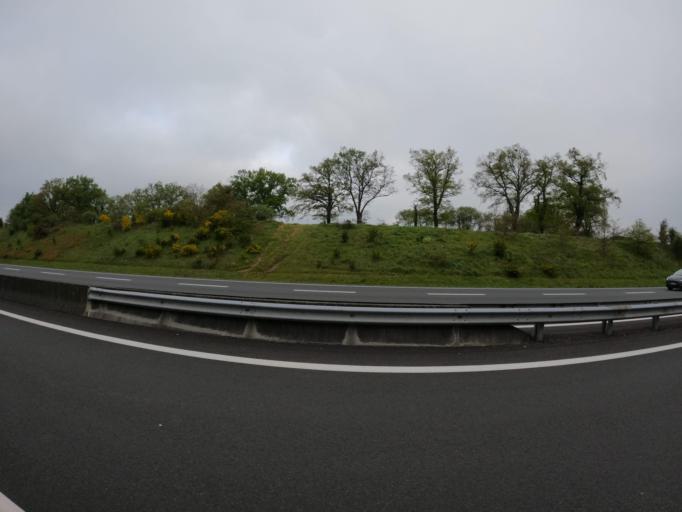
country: FR
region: Pays de la Loire
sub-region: Departement de Maine-et-Loire
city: La Tessoualle
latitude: 47.0146
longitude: -0.8808
